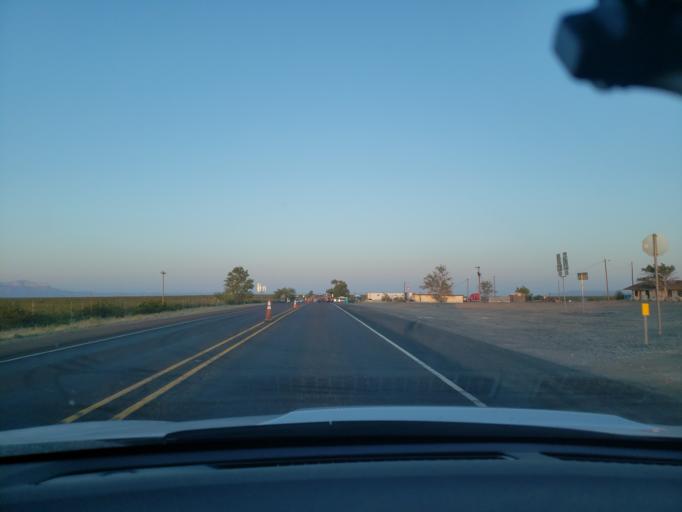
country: US
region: Texas
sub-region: Hudspeth County
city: Sierra Blanca
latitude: 31.7616
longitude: -105.3691
